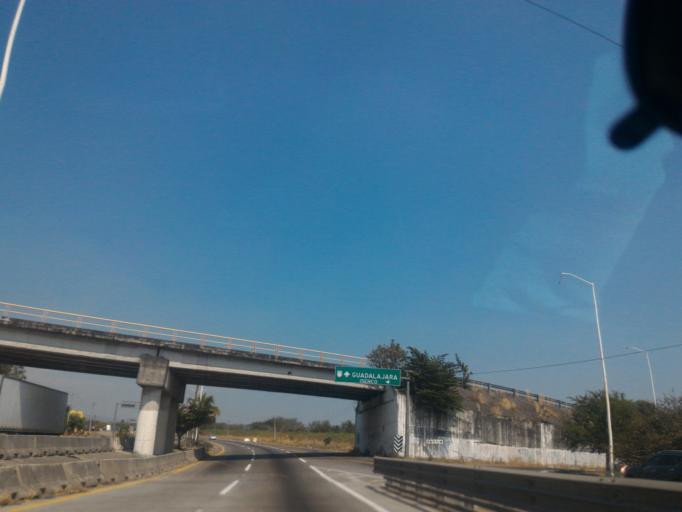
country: MX
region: Colima
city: Colima
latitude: 19.2564
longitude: -103.6853
